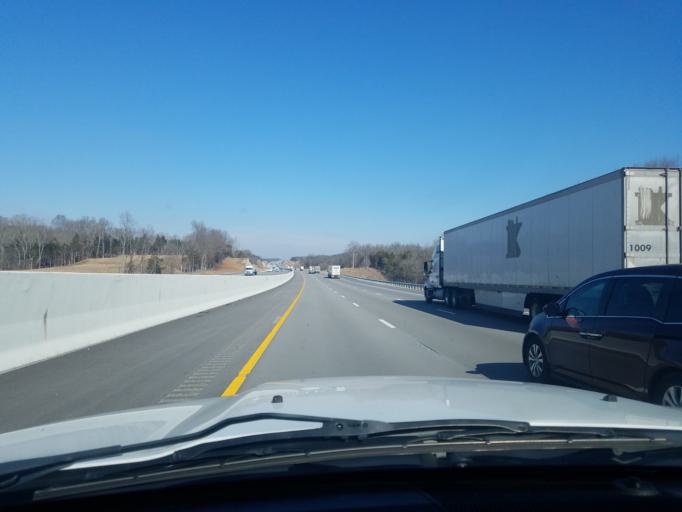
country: US
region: Kentucky
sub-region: Hart County
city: Munfordville
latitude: 37.4076
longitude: -85.8813
